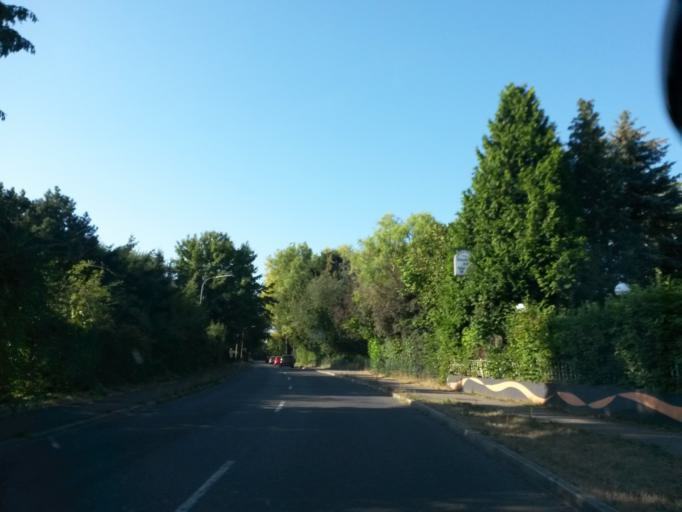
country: DE
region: North Rhine-Westphalia
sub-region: Regierungsbezirk Koln
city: Rosrath
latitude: 50.9150
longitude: 7.1737
